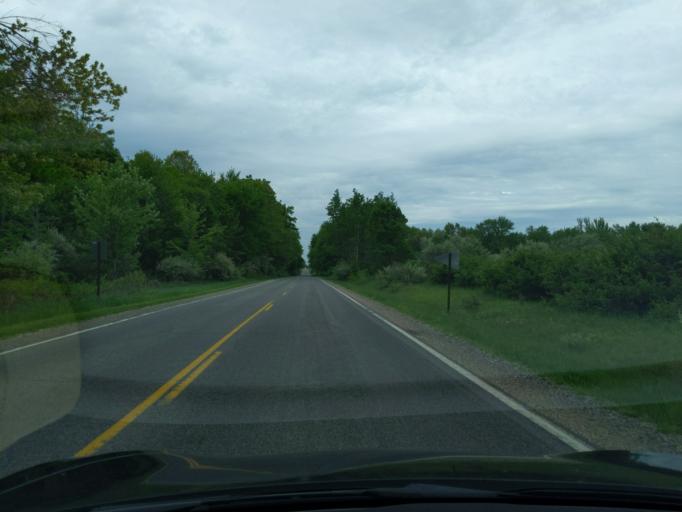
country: US
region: Michigan
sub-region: Ingham County
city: Mason
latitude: 42.5315
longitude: -84.3564
